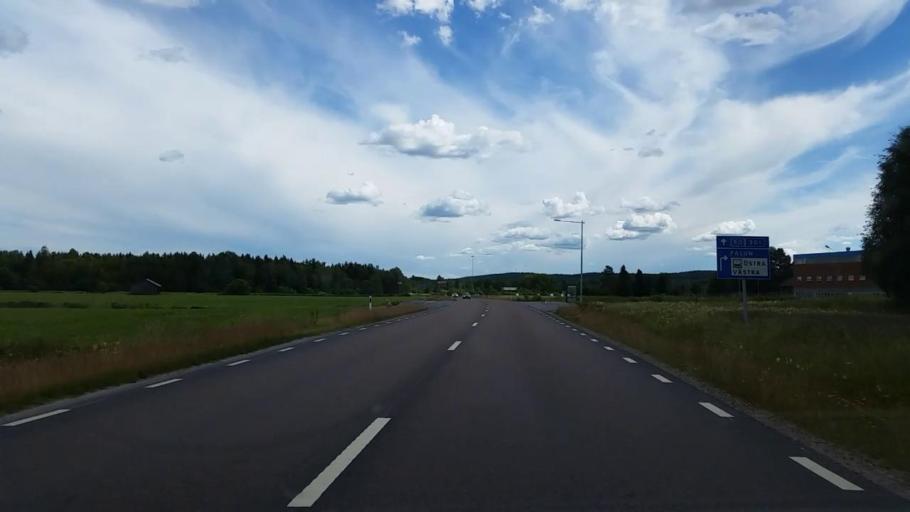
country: SE
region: Gaevleborg
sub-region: Ovanakers Kommun
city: Edsbyn
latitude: 61.3740
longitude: 15.8441
